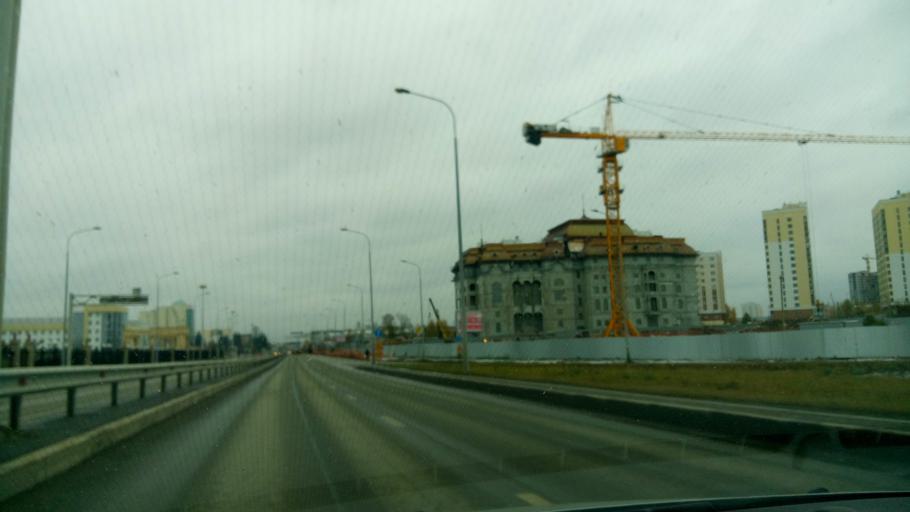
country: RU
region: Sverdlovsk
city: Verkhnyaya Pyshma
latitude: 56.9631
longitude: 60.5836
